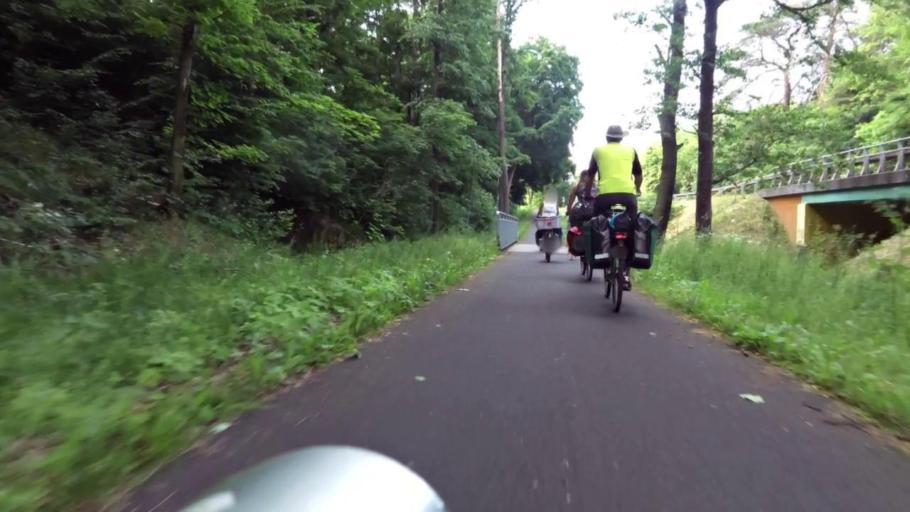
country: PL
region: Kujawsko-Pomorskie
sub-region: Powiat torunski
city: Lysomice
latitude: 53.0804
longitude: 18.5398
